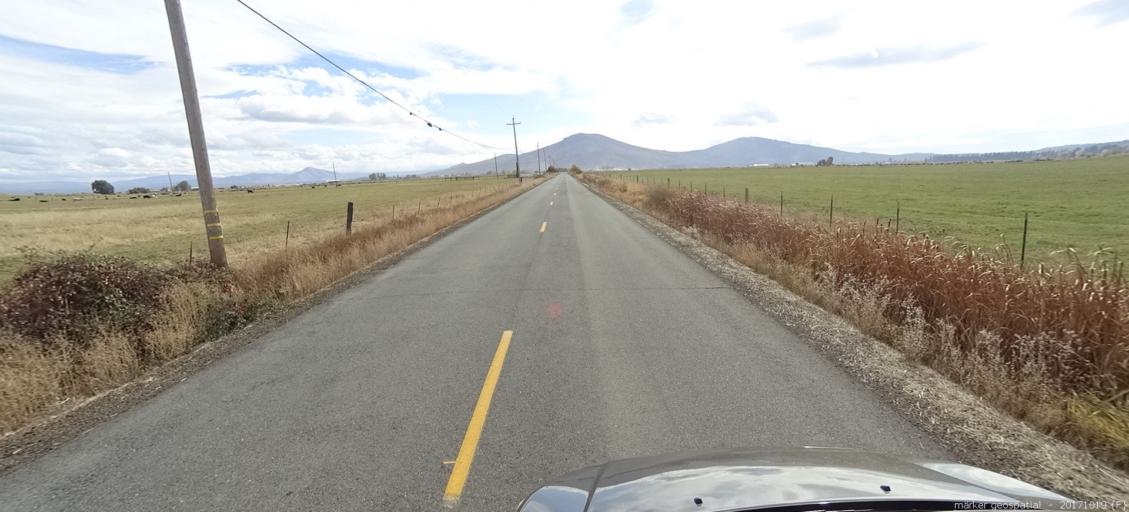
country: US
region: California
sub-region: Shasta County
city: Burney
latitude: 41.0874
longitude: -121.4933
